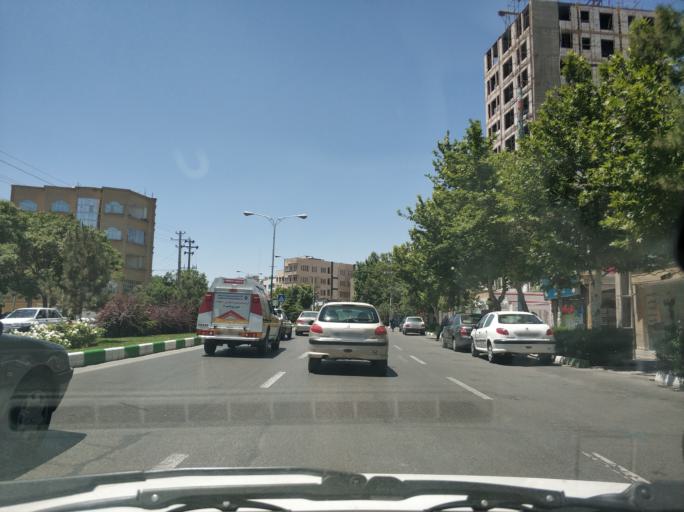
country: IR
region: Razavi Khorasan
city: Mashhad
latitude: 36.3114
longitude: 59.4965
